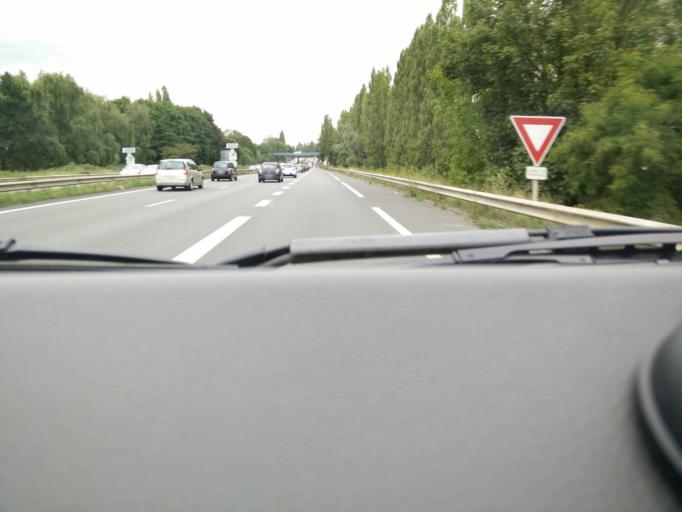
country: FR
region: Nord-Pas-de-Calais
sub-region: Departement du Nord
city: Petite-Foret
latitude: 50.3605
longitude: 3.4859
